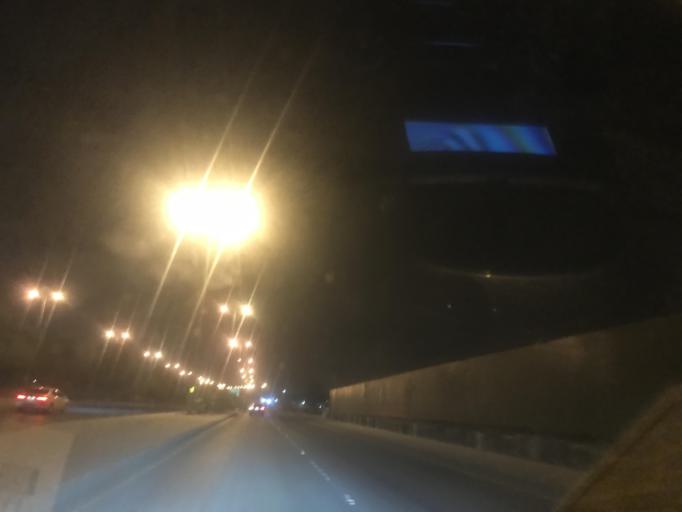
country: SA
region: Ar Riyad
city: Riyadh
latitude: 24.7895
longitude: 46.5890
